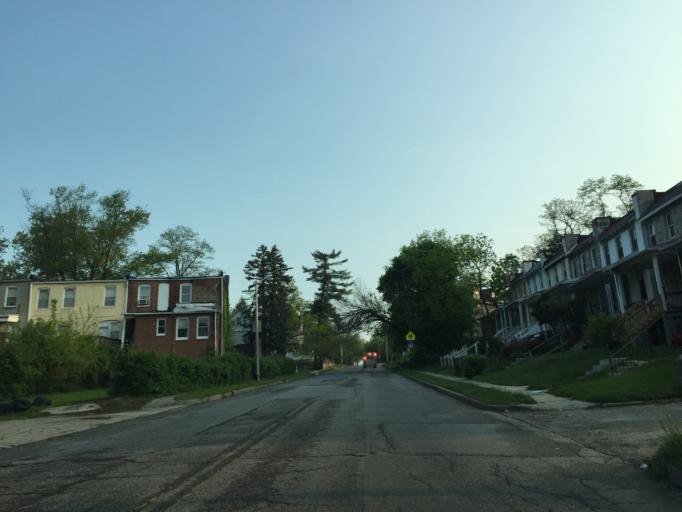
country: US
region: Maryland
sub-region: Baltimore County
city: Lochearn
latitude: 39.3168
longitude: -76.6728
